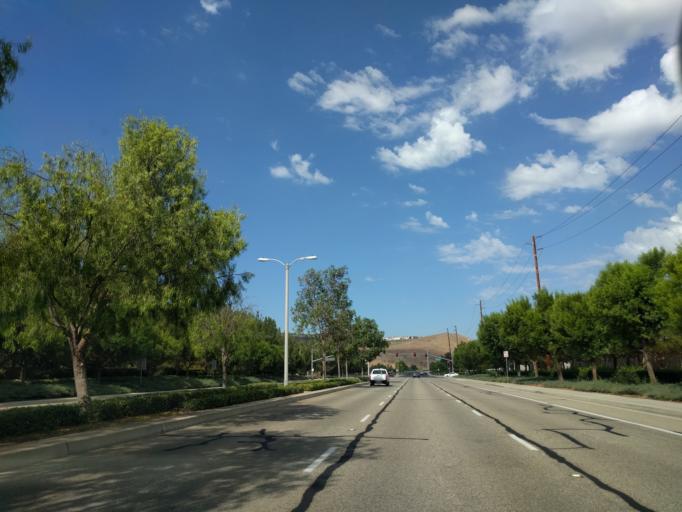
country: US
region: California
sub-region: Orange County
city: Laguna Woods
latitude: 33.6306
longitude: -117.7381
